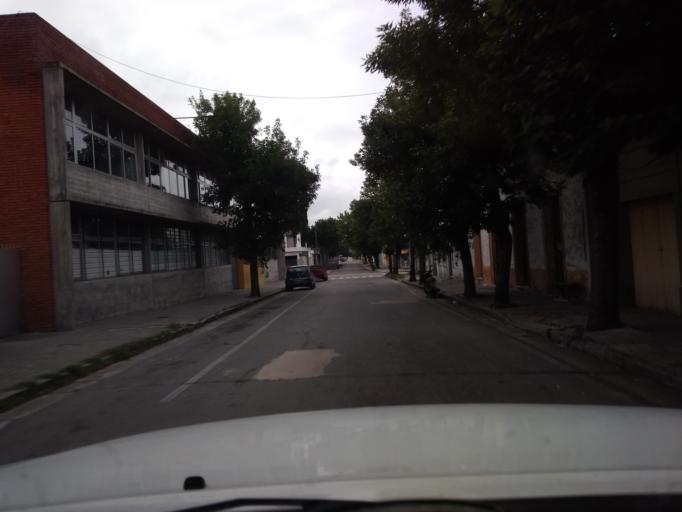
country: UY
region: Florida
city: Florida
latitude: -34.1018
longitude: -56.2144
